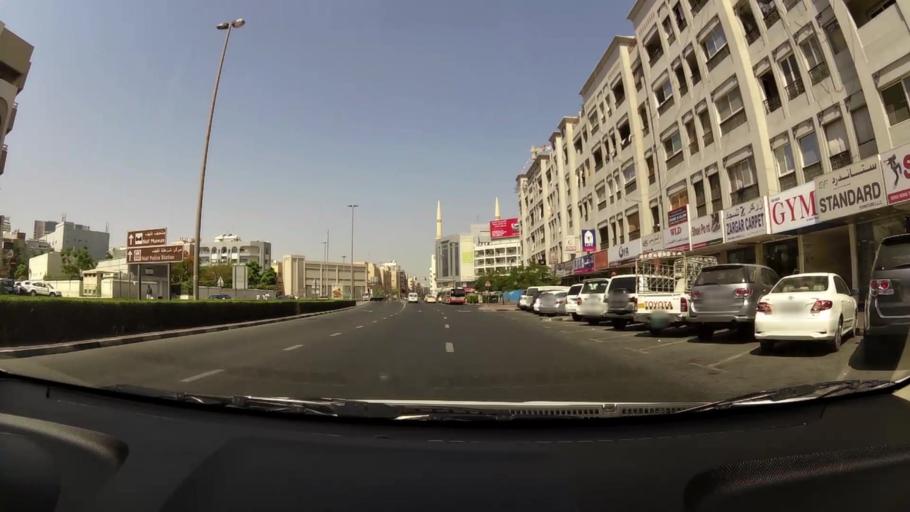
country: AE
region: Ash Shariqah
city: Sharjah
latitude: 25.2741
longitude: 55.3076
